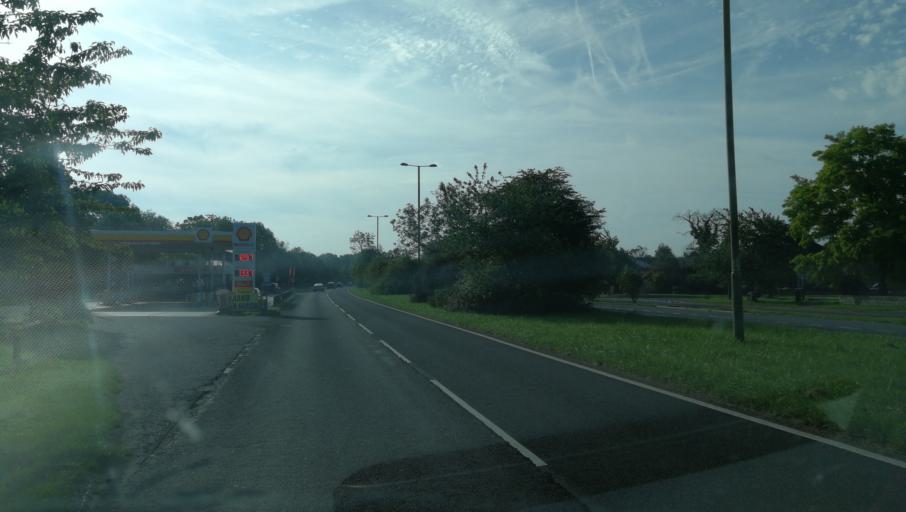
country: GB
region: England
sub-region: Oxfordshire
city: Yarnton
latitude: 51.8106
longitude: -1.3074
